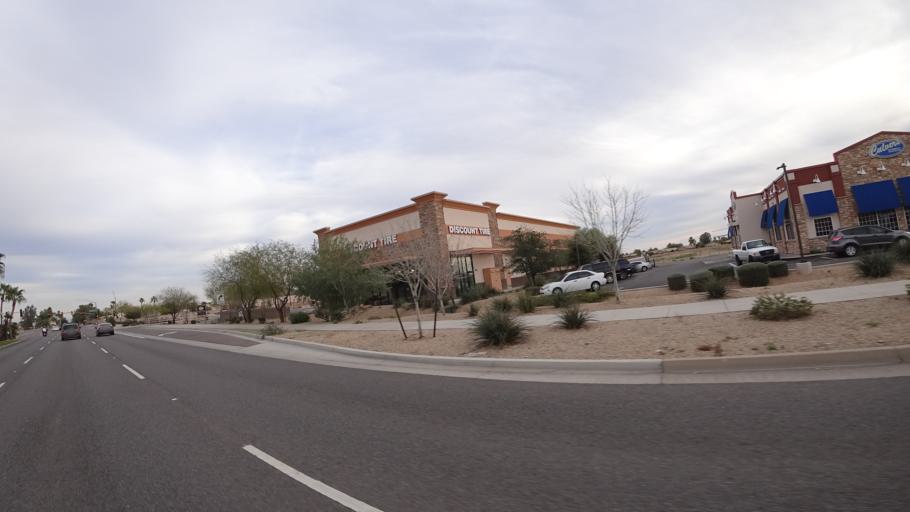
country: US
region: Arizona
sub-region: Maricopa County
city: Sun City West
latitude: 33.6387
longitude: -112.4066
